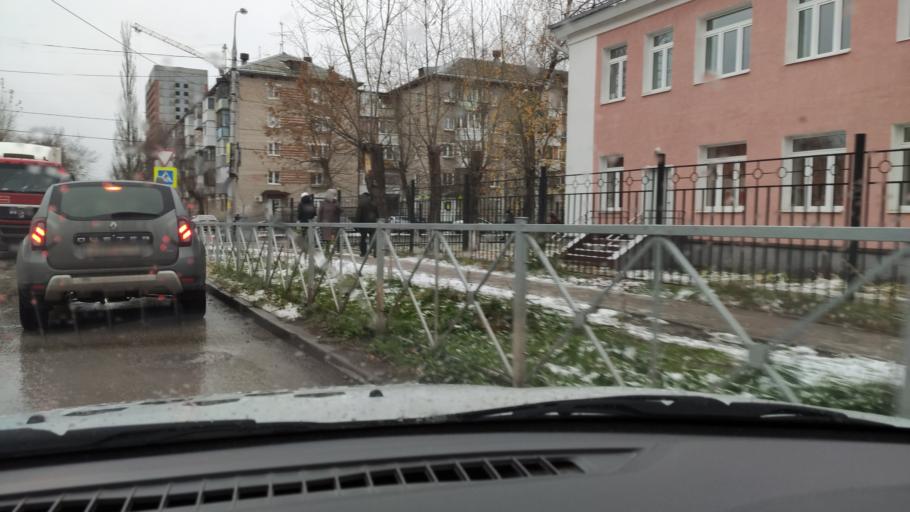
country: RU
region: Perm
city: Perm
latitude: 57.9661
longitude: 56.2327
